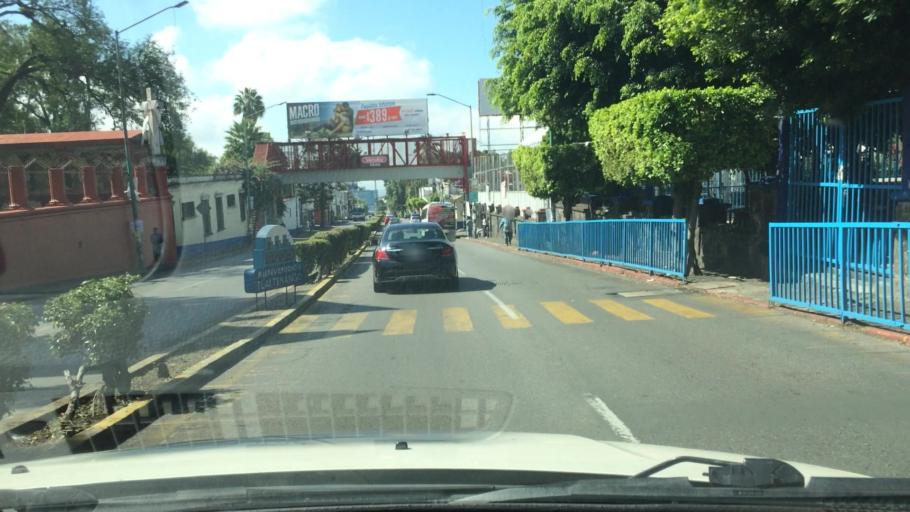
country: MX
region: Morelos
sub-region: Cuernavaca
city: Fraccionamiento Lomas de Ahuatlan
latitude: 18.9471
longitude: -99.2439
